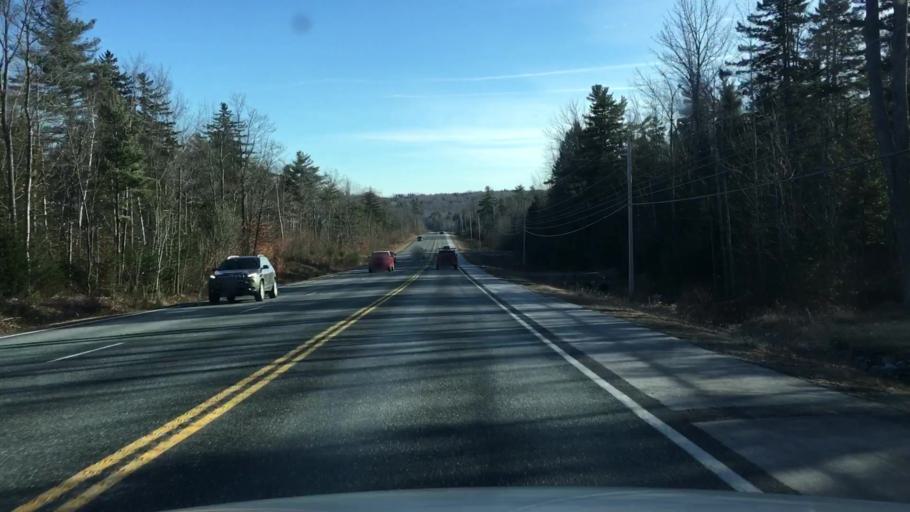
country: US
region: Maine
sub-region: Hancock County
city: Dedham
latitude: 44.6409
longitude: -68.5520
